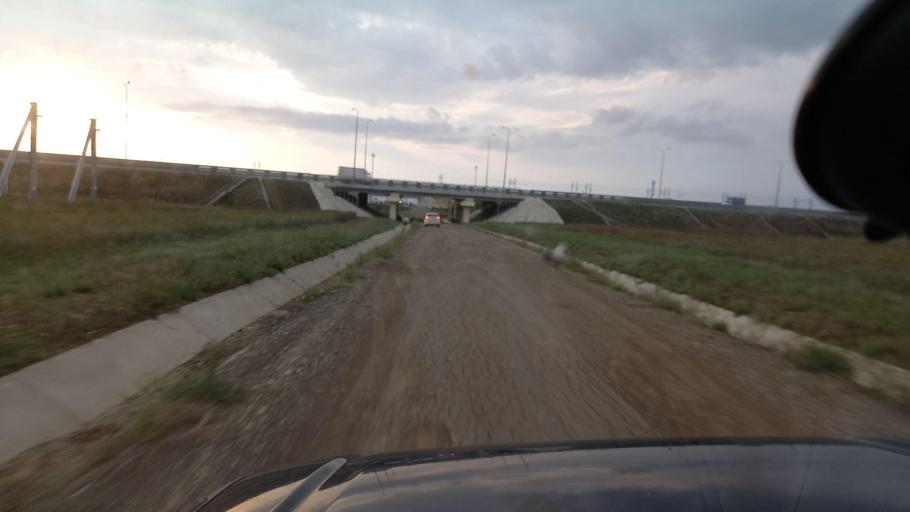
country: RU
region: Krasnodarskiy
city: Taman'
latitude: 45.2144
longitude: 36.7629
